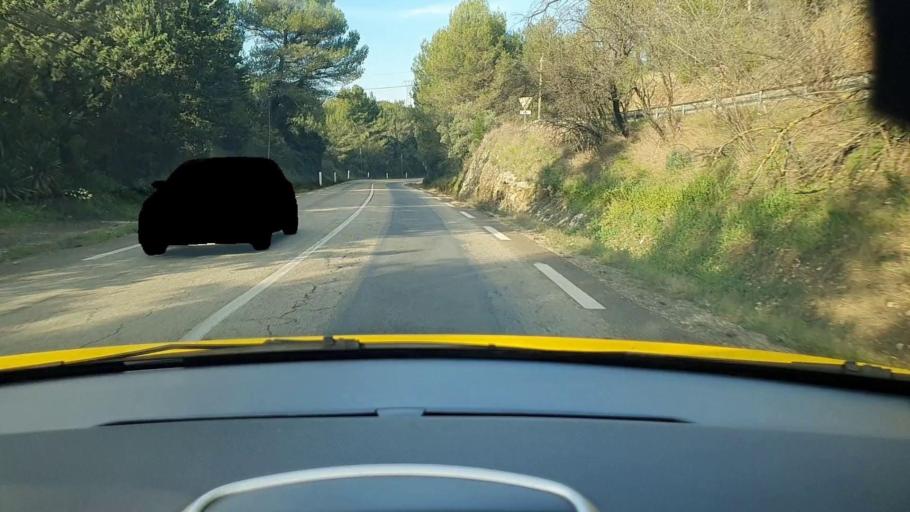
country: FR
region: Languedoc-Roussillon
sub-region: Departement du Gard
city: Comps
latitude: 43.8245
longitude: 4.5956
